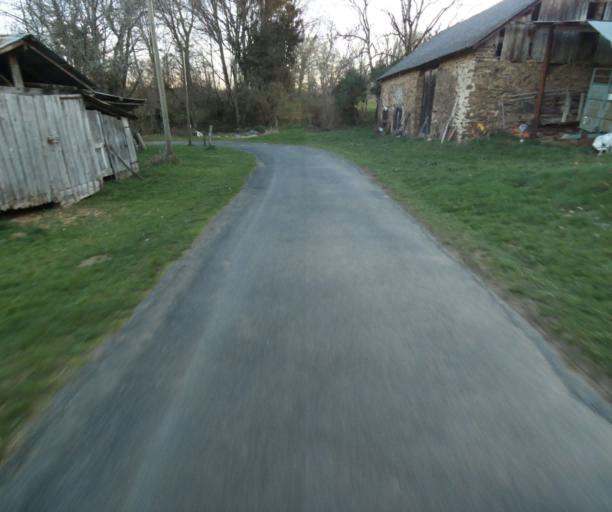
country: FR
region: Limousin
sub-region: Departement de la Correze
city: Saint-Mexant
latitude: 45.2951
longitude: 1.5923
